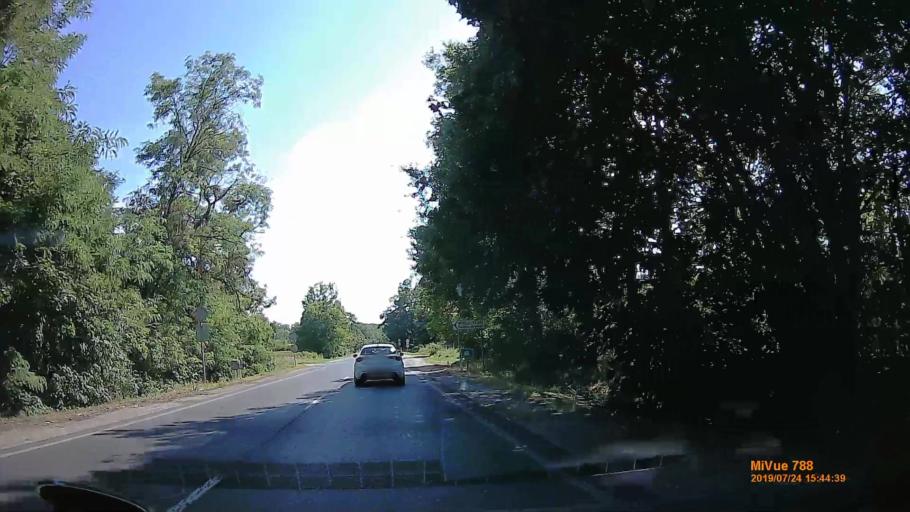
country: HU
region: Szabolcs-Szatmar-Bereg
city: Vasarosnameny
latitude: 48.0972
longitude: 22.2914
